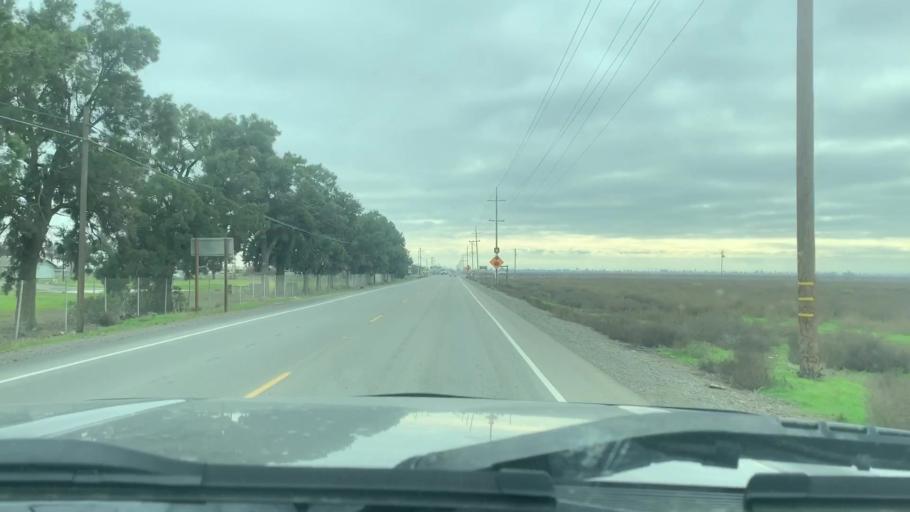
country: US
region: California
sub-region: Merced County
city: Los Banos
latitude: 37.1025
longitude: -120.8349
